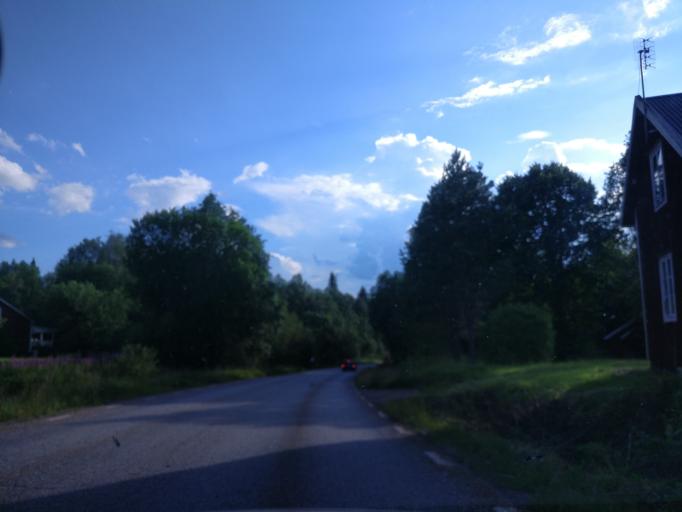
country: SE
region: Dalarna
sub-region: Ludvika Kommun
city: Ludvika
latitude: 60.2657
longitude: 15.0584
